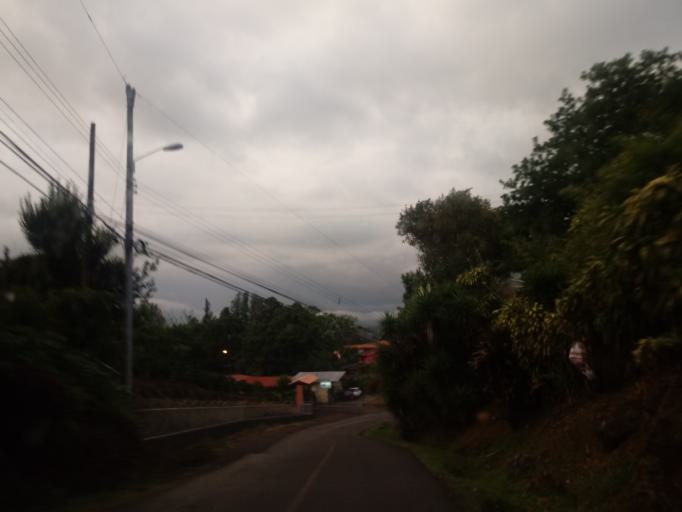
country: CR
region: Heredia
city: Angeles
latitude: 10.0264
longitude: -84.0402
